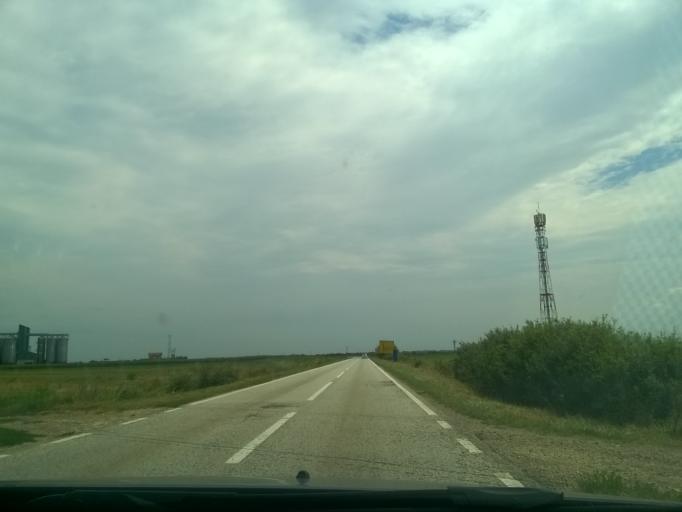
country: RS
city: Banatski Despotovac
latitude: 45.3785
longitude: 20.6715
